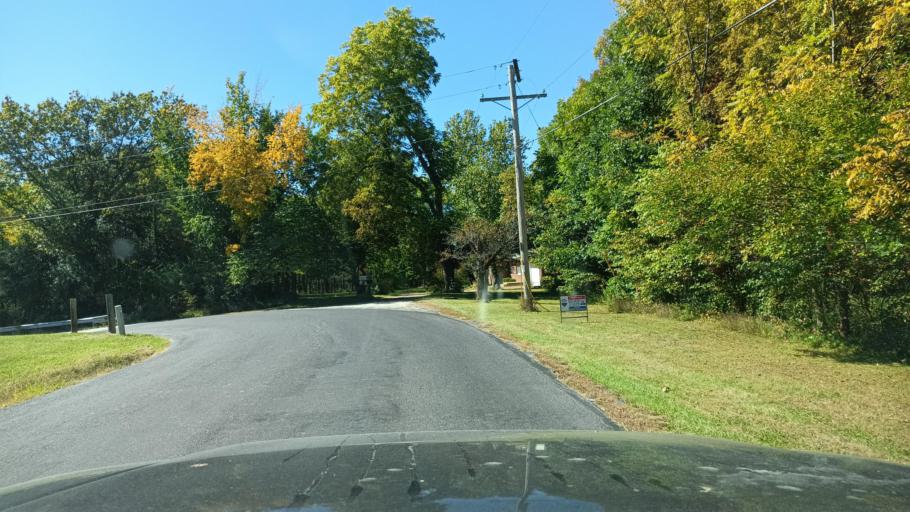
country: US
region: Illinois
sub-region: Champaign County
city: Lake of the Woods
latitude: 40.2150
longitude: -88.3546
